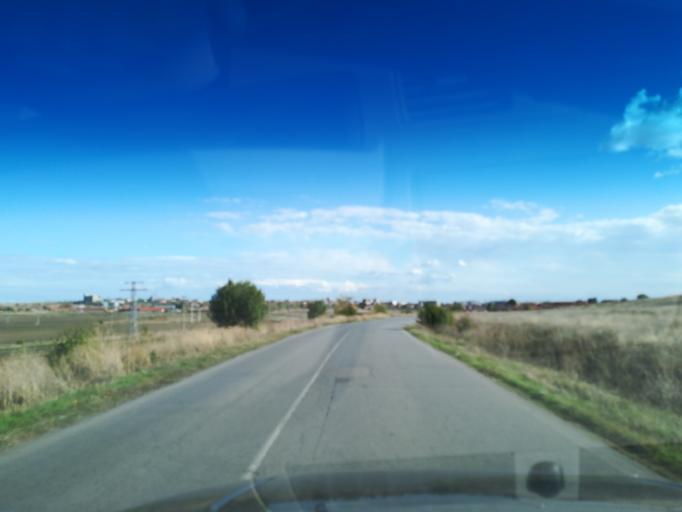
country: BG
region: Stara Zagora
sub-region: Obshtina Chirpan
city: Chirpan
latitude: 42.2069
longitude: 25.3060
